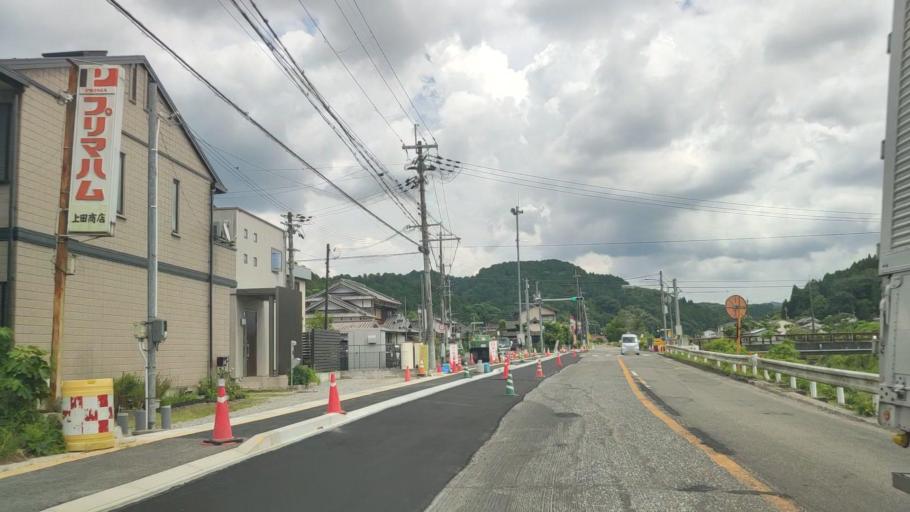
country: JP
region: Hyogo
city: Yamazakicho-nakabirose
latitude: 34.9795
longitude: 134.4423
